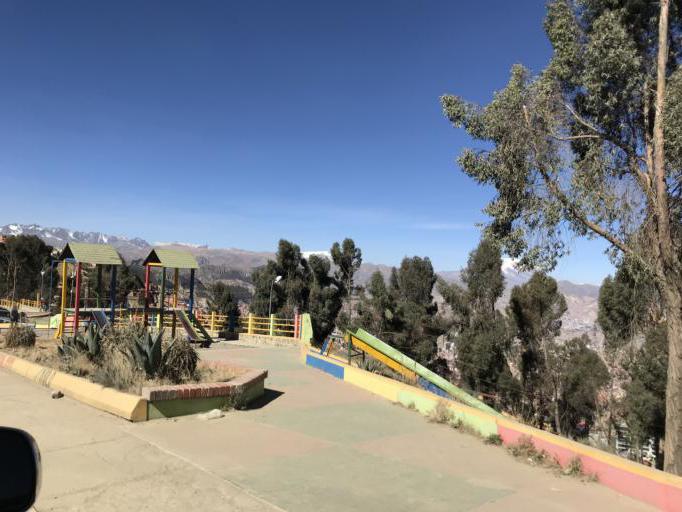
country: BO
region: La Paz
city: La Paz
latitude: -16.4864
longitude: -68.1697
